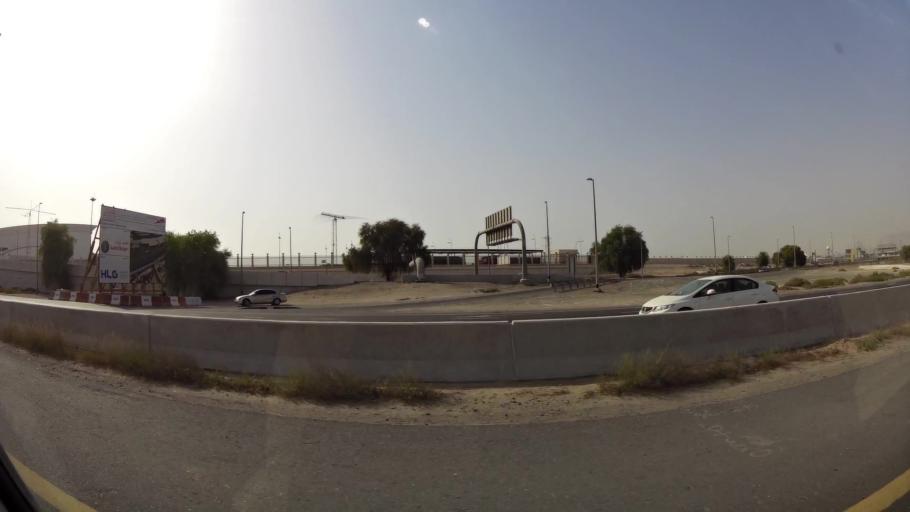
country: AE
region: Ash Shariqah
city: Sharjah
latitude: 25.2308
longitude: 55.3983
